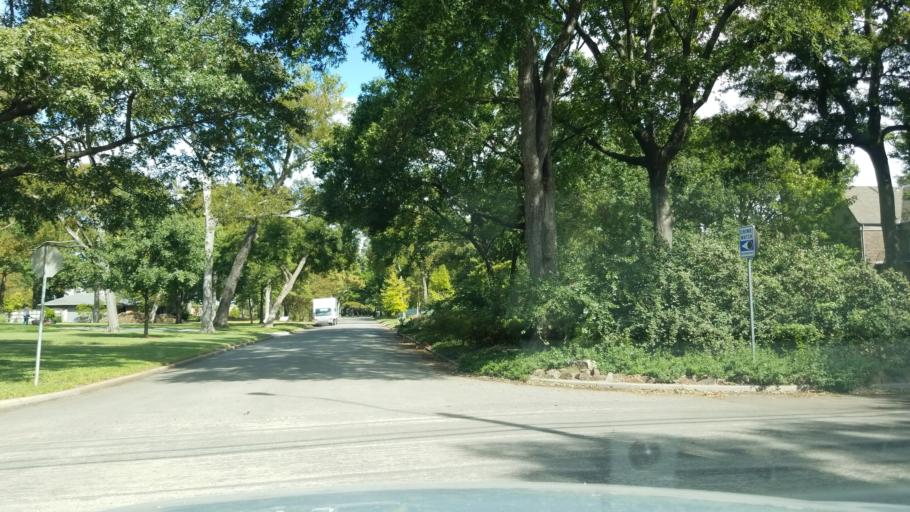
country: US
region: Texas
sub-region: Dallas County
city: Highland Park
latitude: 32.8116
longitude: -96.7180
